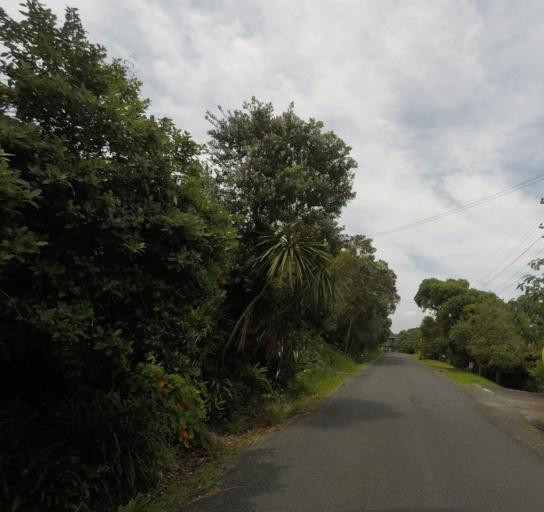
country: NZ
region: Auckland
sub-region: Auckland
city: Warkworth
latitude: -36.2964
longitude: 174.7992
